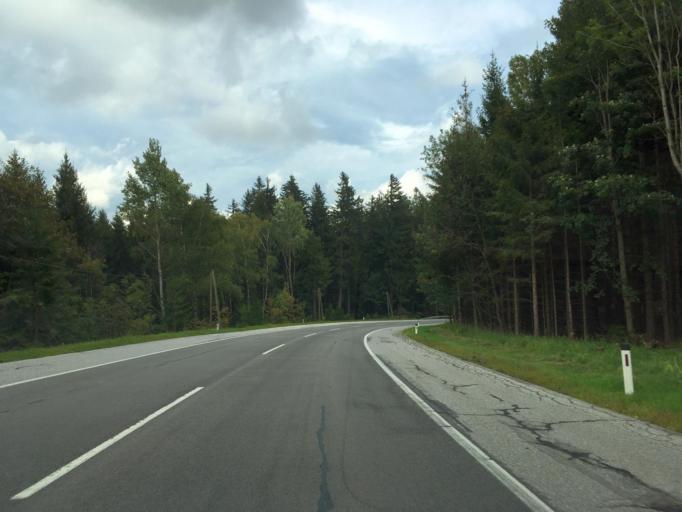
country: AT
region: Lower Austria
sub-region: Politischer Bezirk Neunkirchen
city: Monichkirchen
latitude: 47.5182
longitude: 16.0564
